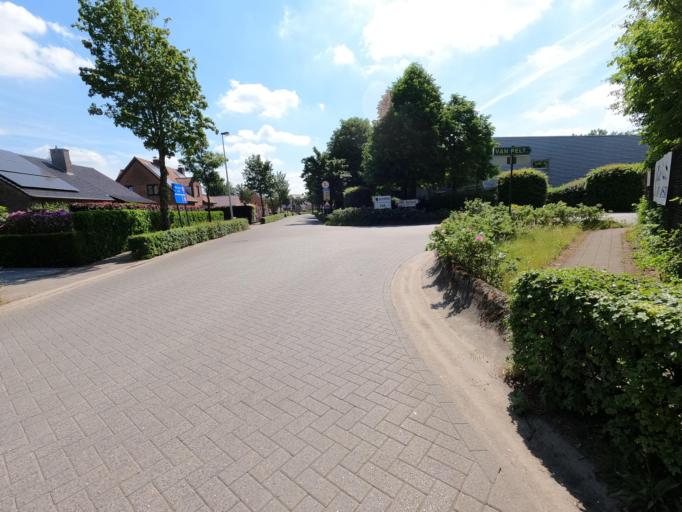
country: BE
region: Flanders
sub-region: Provincie Antwerpen
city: Schilde
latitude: 51.2698
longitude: 4.6221
